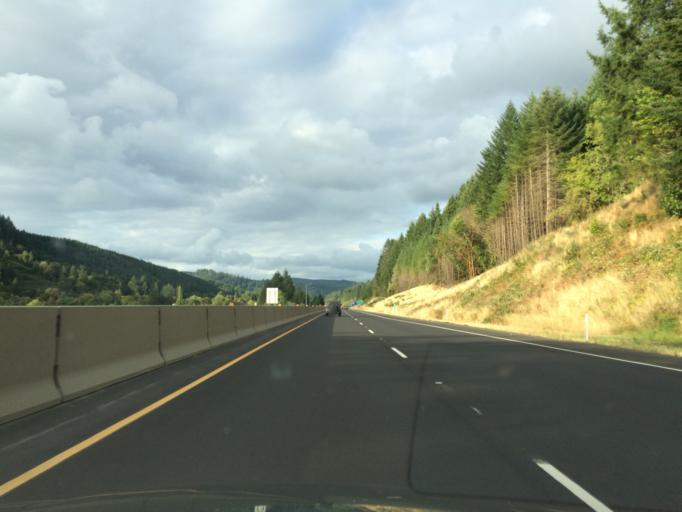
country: US
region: Oregon
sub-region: Douglas County
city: Drain
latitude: 43.7155
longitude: -123.2148
